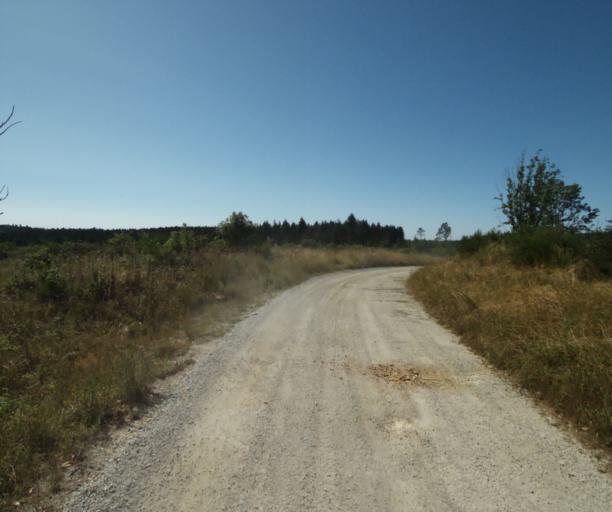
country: FR
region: Midi-Pyrenees
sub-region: Departement du Tarn
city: Soreze
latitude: 43.4241
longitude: 2.1214
